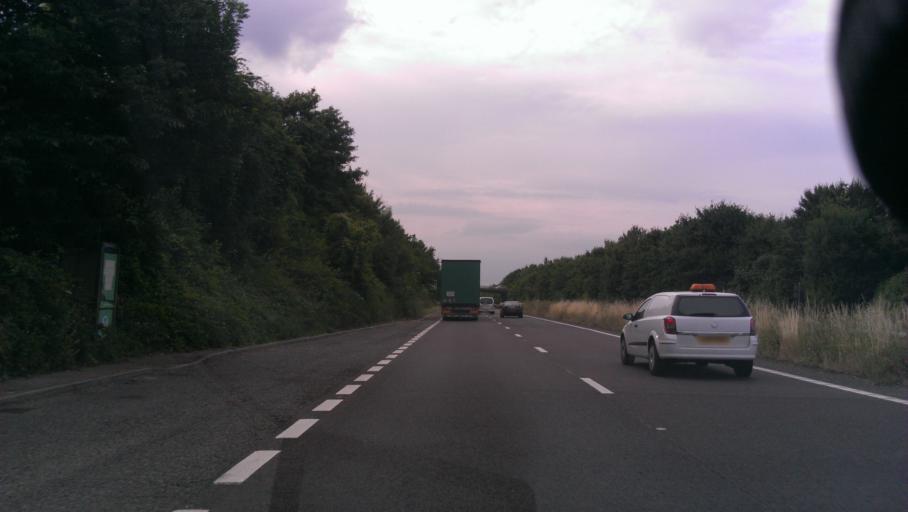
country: GB
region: England
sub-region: Kent
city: Canterbury
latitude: 51.2598
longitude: 1.0755
